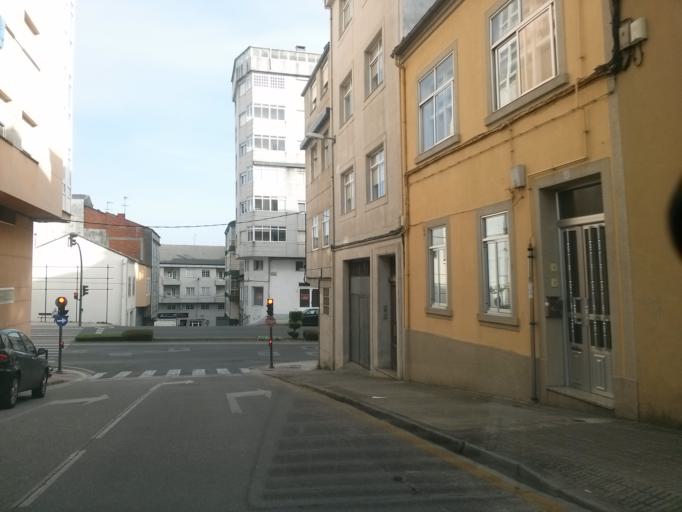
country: ES
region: Galicia
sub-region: Provincia de Lugo
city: Lugo
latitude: 43.0100
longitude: -7.5694
